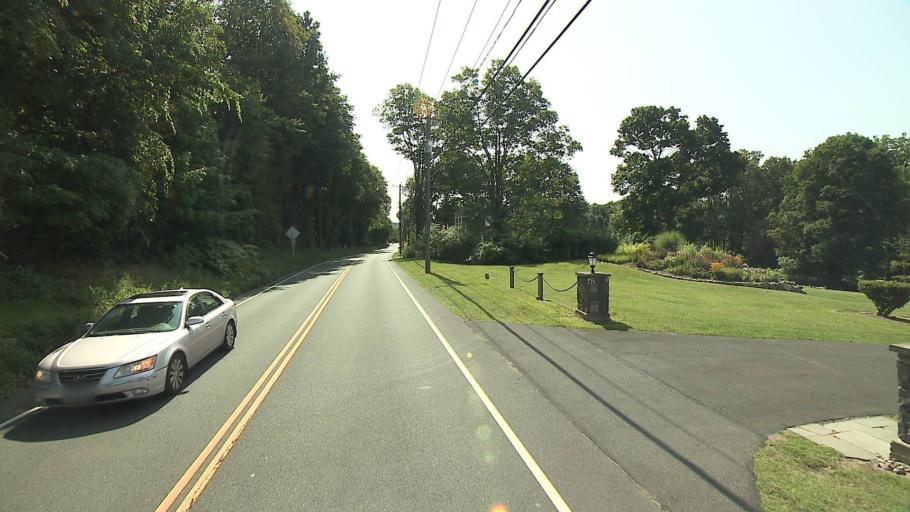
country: US
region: Connecticut
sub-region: Fairfield County
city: Newtown
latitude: 41.4431
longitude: -73.3734
